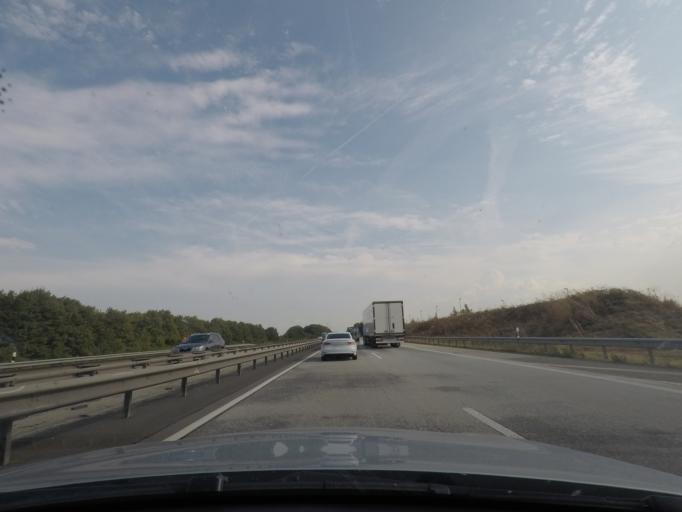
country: DE
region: Rheinland-Pfalz
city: Zotzenheim
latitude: 49.8665
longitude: 7.9642
